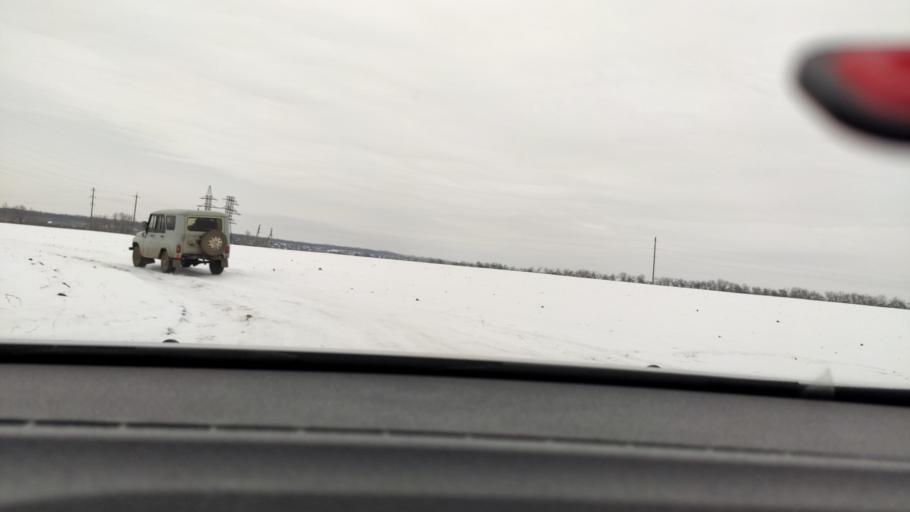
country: RU
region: Voronezj
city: Semiluki
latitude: 51.7108
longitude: 38.9785
